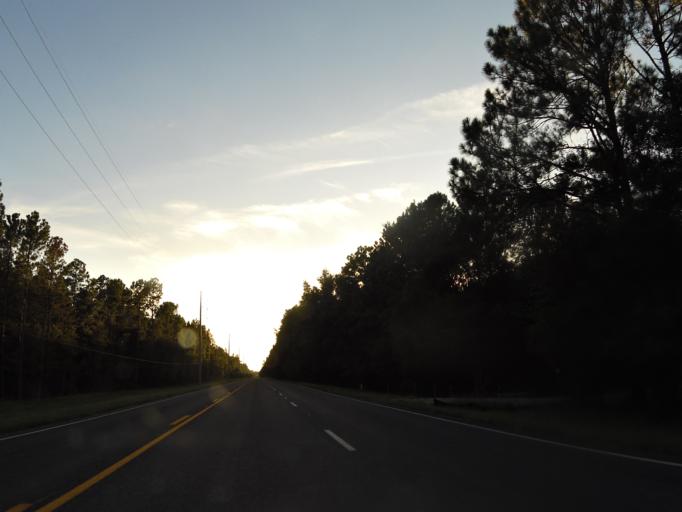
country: US
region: Georgia
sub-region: Camden County
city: Woodbine
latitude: 31.1042
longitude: -81.6869
